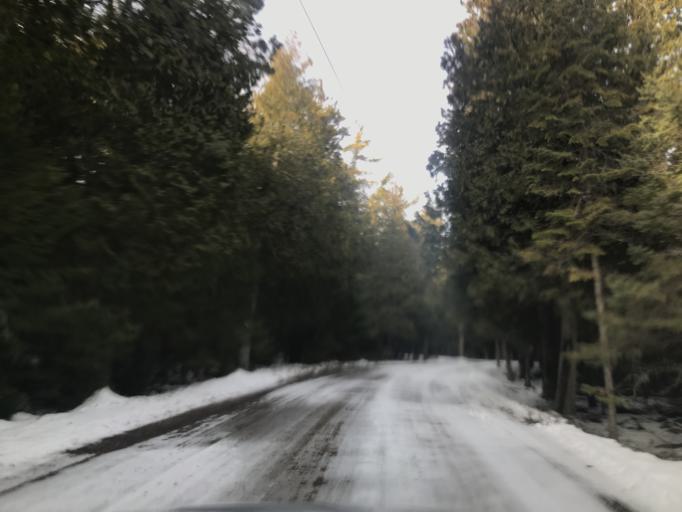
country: US
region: Wisconsin
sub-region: Door County
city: Sturgeon Bay
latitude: 45.1403
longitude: -87.0485
